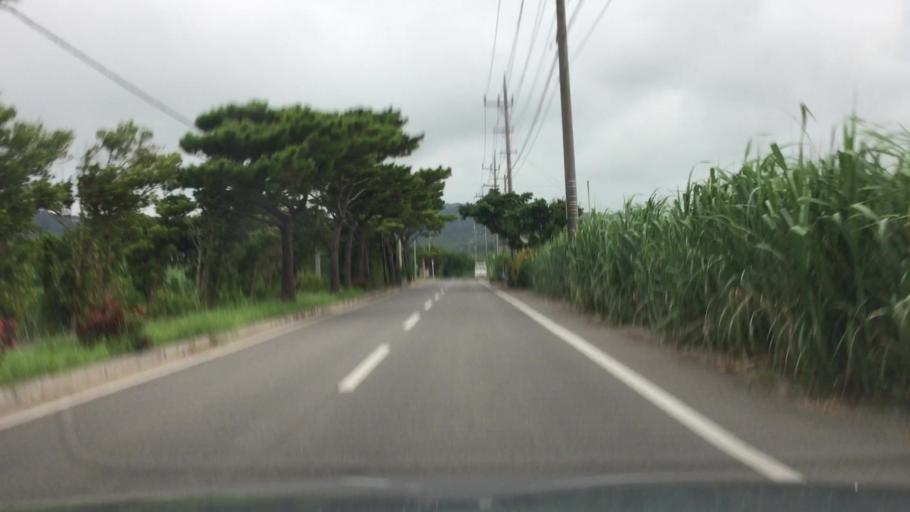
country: JP
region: Okinawa
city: Ishigaki
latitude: 24.3920
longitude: 124.1554
